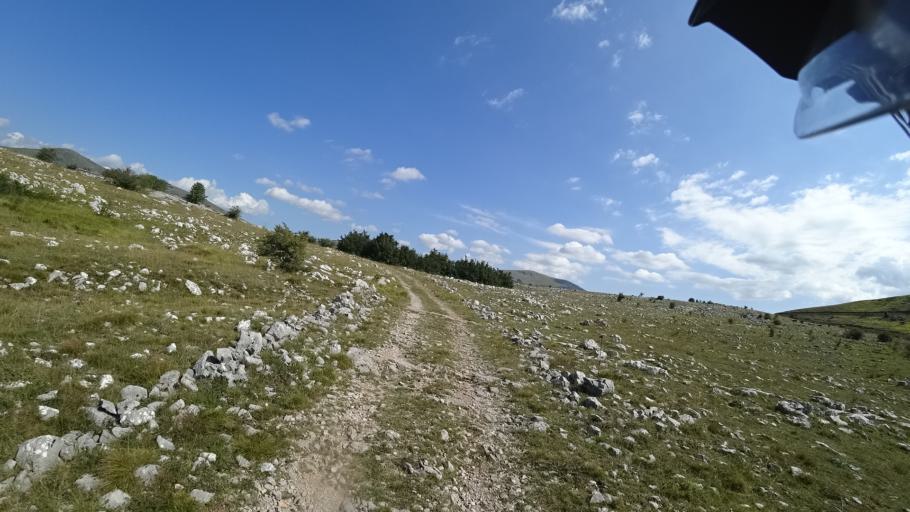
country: HR
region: Zadarska
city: Gracac
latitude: 44.3700
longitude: 15.9574
